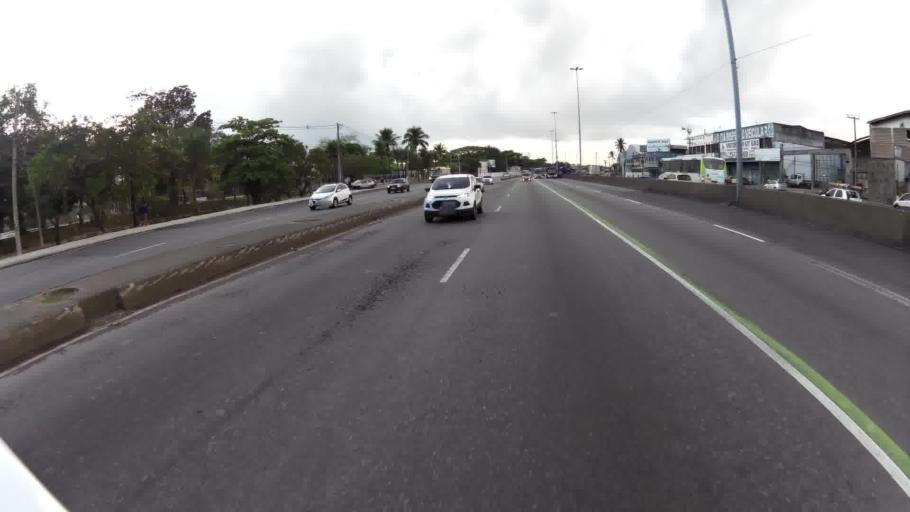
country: BR
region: Rio de Janeiro
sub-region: Duque De Caxias
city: Duque de Caxias
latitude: -22.8372
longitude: -43.2574
